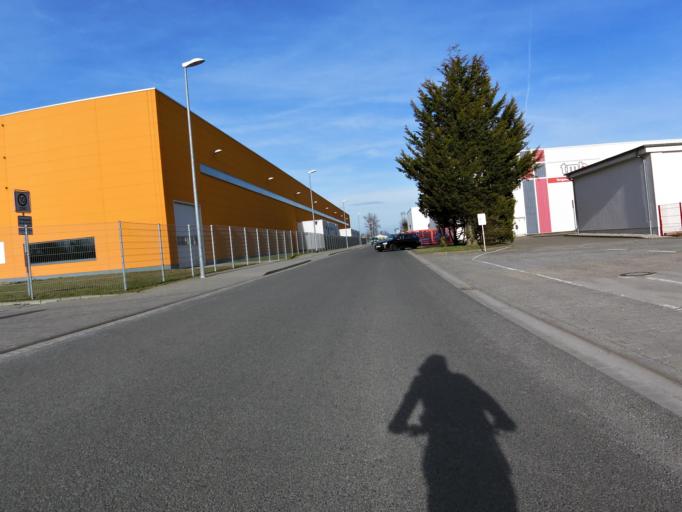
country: DE
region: Saxony
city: Torgau
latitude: 51.5716
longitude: 13.0004
